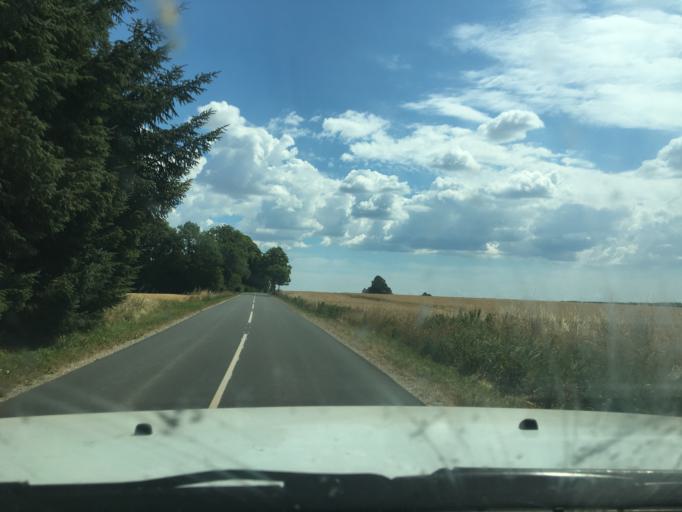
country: DK
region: Central Jutland
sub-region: Syddjurs Kommune
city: Hornslet
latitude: 56.3414
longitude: 10.2690
